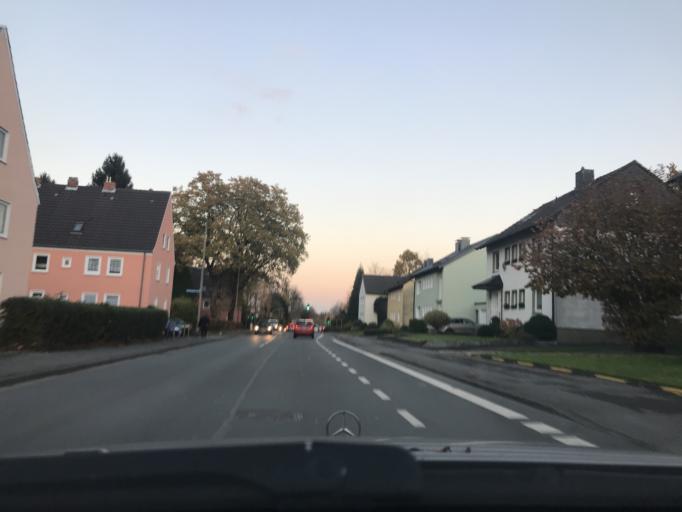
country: DE
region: North Rhine-Westphalia
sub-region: Regierungsbezirk Arnsberg
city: Soest
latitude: 51.5566
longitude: 8.1272
